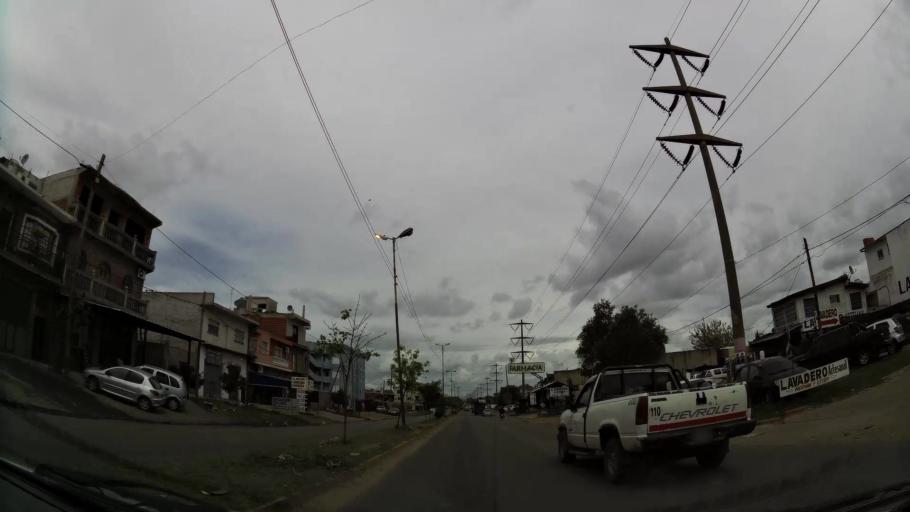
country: AR
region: Buenos Aires
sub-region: Partido de Quilmes
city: Quilmes
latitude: -34.7574
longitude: -58.2571
